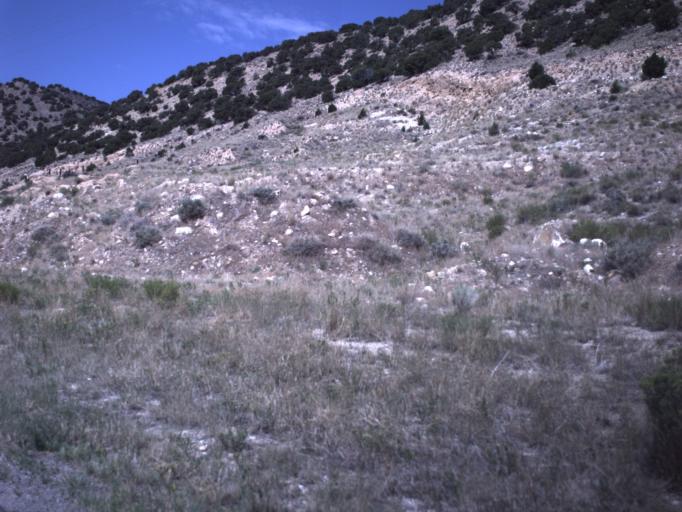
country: US
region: Utah
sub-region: Daggett County
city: Manila
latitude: 40.9815
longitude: -109.7445
